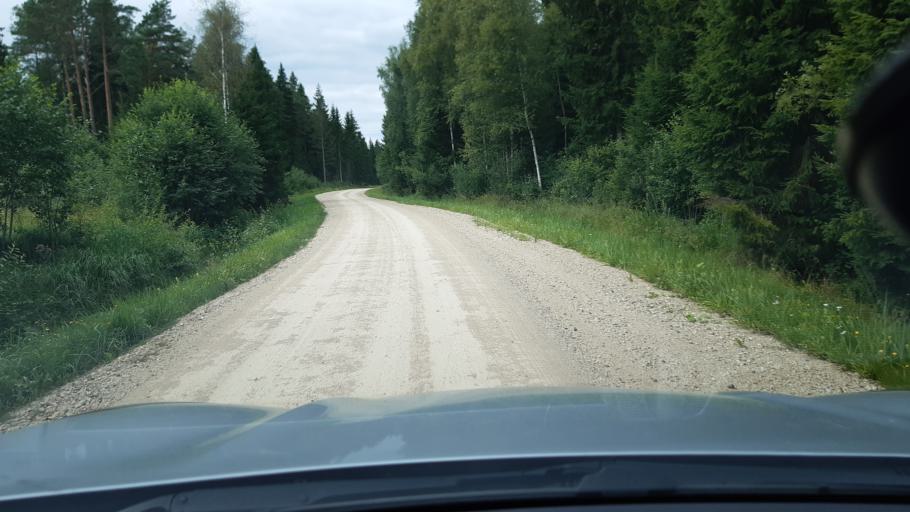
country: EE
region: Raplamaa
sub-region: Jaervakandi vald
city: Jarvakandi
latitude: 58.8069
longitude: 24.8318
